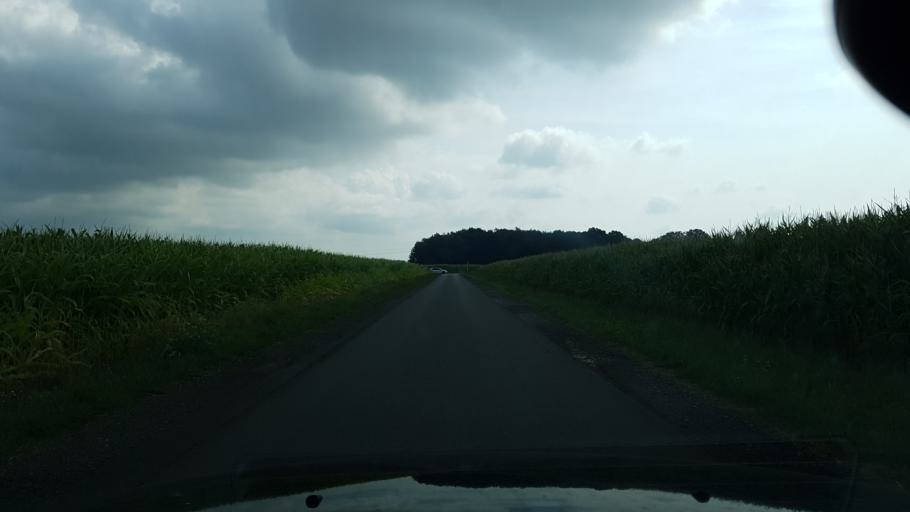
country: DE
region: Lower Saxony
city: Sulingen
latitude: 52.6794
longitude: 8.7635
